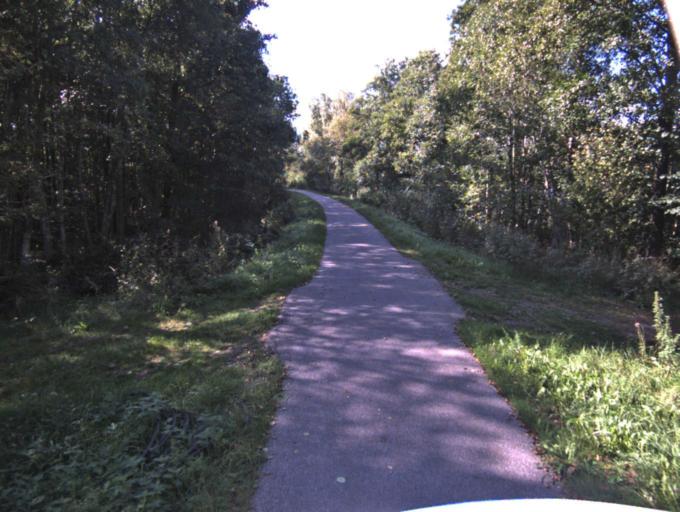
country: SE
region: Vaestra Goetaland
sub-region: Ulricehamns Kommun
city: Ulricehamn
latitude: 57.8451
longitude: 13.2977
